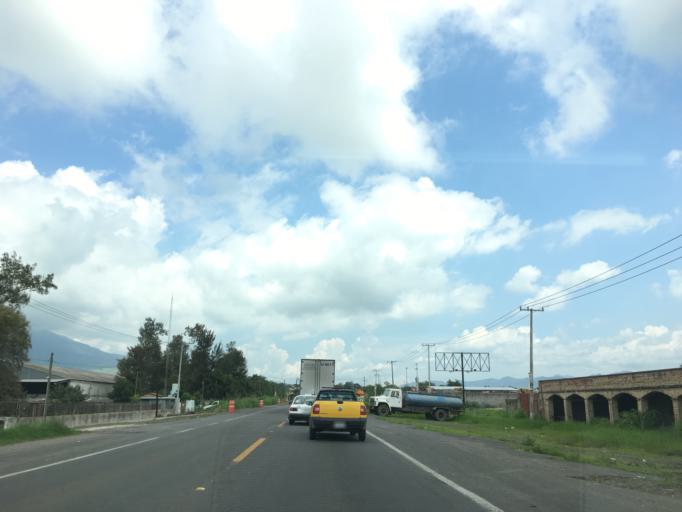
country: MX
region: Nayarit
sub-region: Tepic
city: La Corregidora
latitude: 21.4573
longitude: -104.8244
